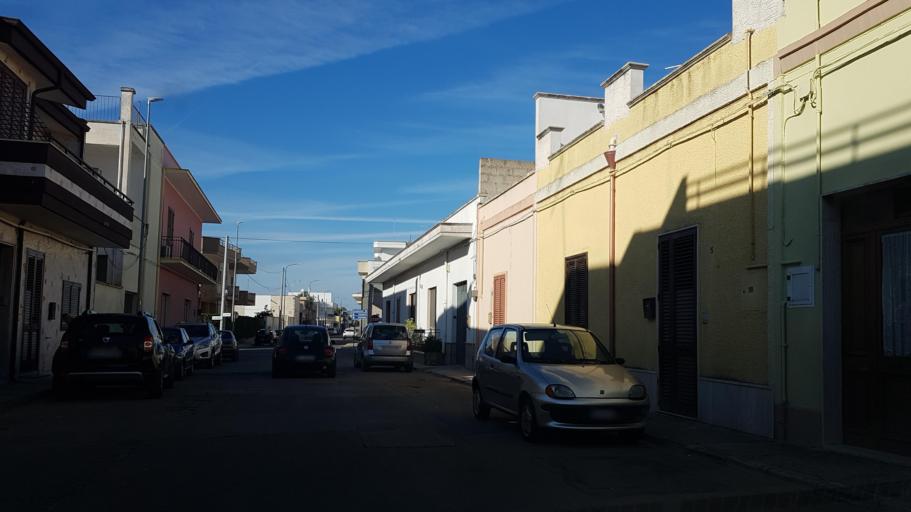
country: IT
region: Apulia
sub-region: Provincia di Lecce
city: Salice Salentino
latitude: 40.3874
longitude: 17.9579
